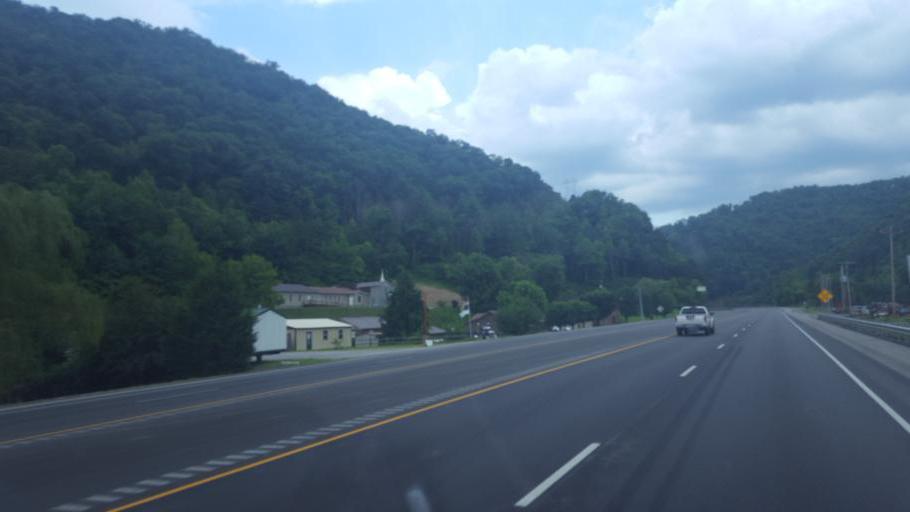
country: US
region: Kentucky
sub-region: Pike County
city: Pikeville
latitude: 37.3590
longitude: -82.5551
